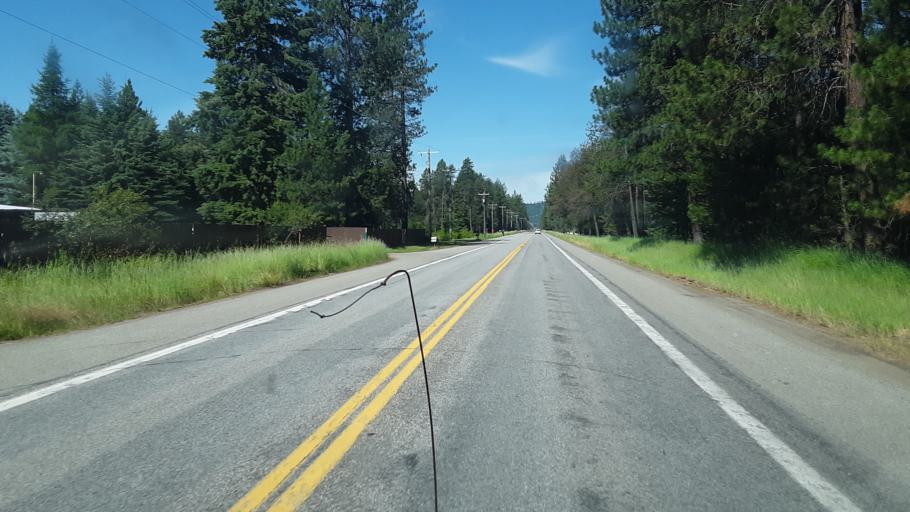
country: US
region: Idaho
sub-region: Kootenai County
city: Rathdrum
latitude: 47.8172
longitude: -116.8319
